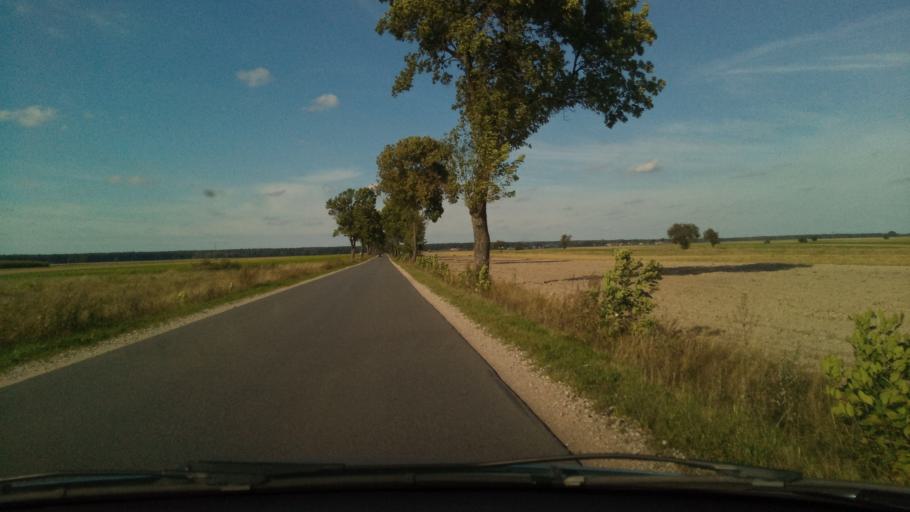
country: PL
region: Lodz Voivodeship
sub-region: Powiat piotrkowski
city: Sulejow
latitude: 51.3858
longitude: 19.8192
